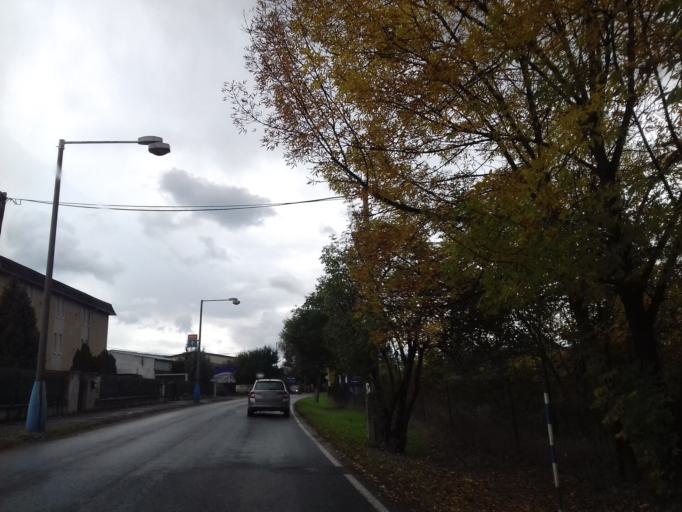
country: CZ
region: Central Bohemia
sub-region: Okres Praha-Zapad
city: Dobrichovice
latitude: 49.9355
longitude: 14.2830
